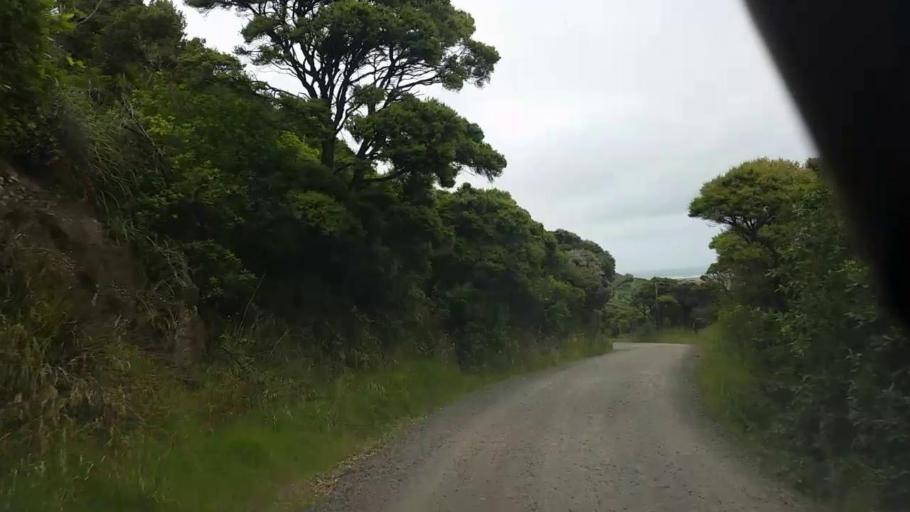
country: NZ
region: Auckland
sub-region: Auckland
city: Titirangi
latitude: -37.0350
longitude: 174.5154
